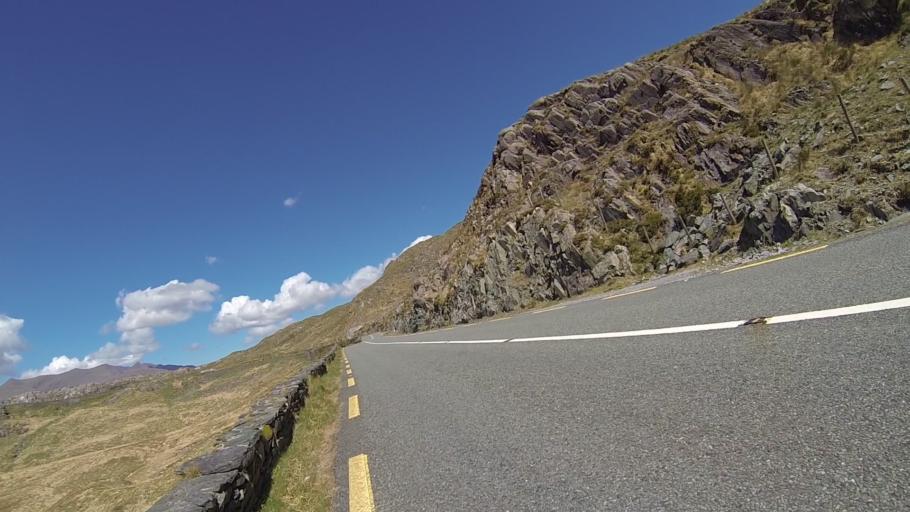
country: IE
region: Munster
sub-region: Ciarrai
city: Kenmare
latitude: 51.9350
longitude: -9.6529
